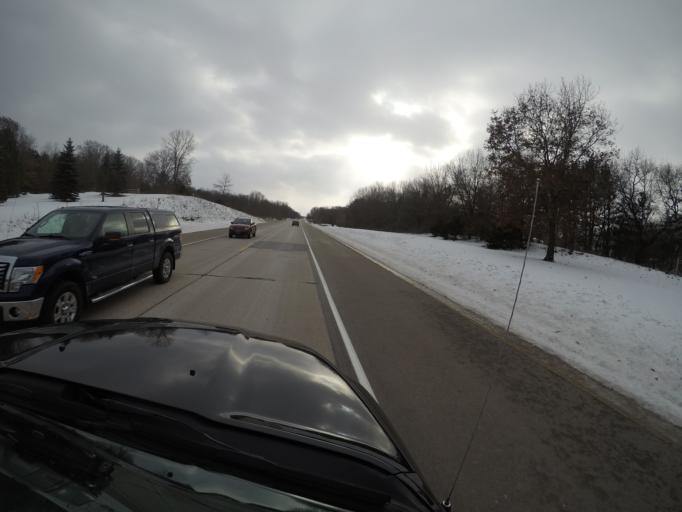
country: US
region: Wisconsin
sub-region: Trempealeau County
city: Galesville
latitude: 44.0437
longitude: -91.2908
